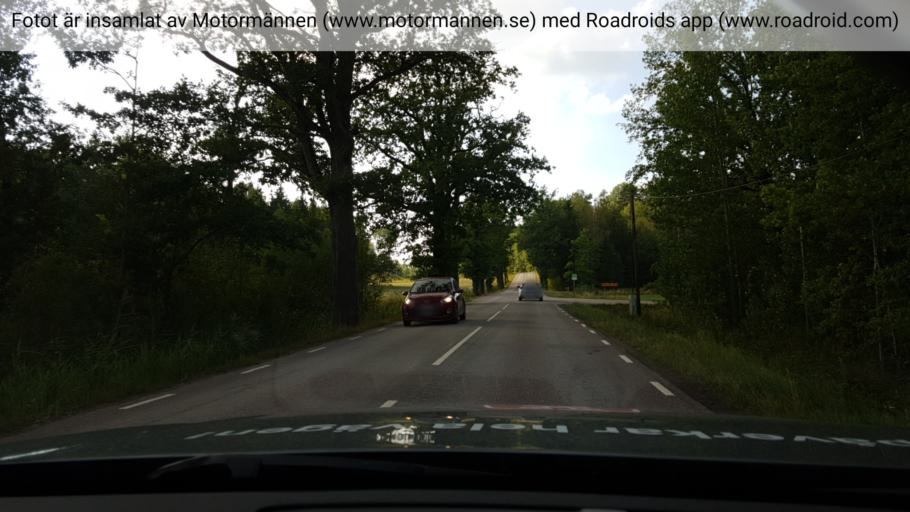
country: SE
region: Soedermanland
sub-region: Gnesta Kommun
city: Gnesta
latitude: 59.0839
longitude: 17.2622
